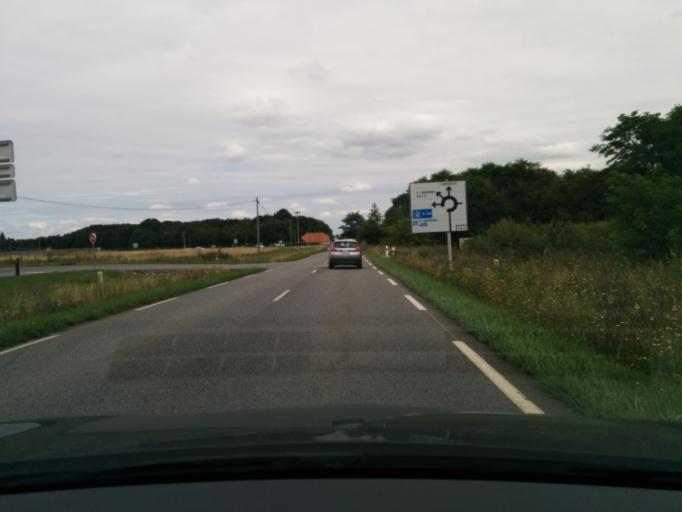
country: FR
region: Midi-Pyrenees
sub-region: Departement des Hautes-Pyrenees
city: La Barthe-de-Neste
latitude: 43.0912
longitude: 0.3873
